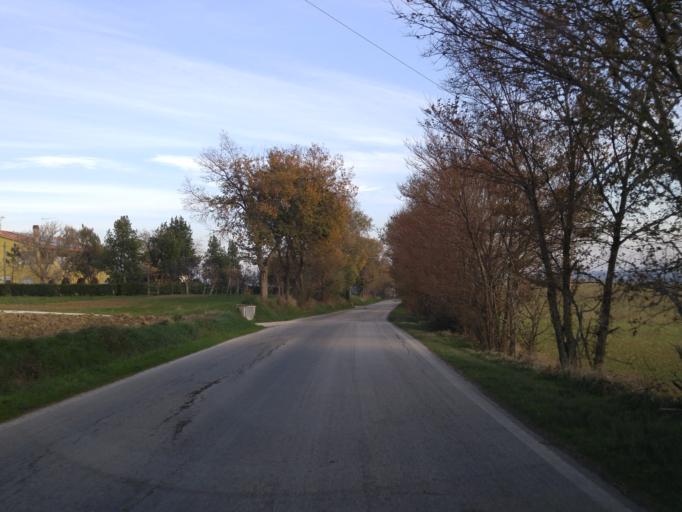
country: IT
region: The Marches
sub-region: Provincia di Pesaro e Urbino
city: Lucrezia
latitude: 43.7945
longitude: 12.9319
